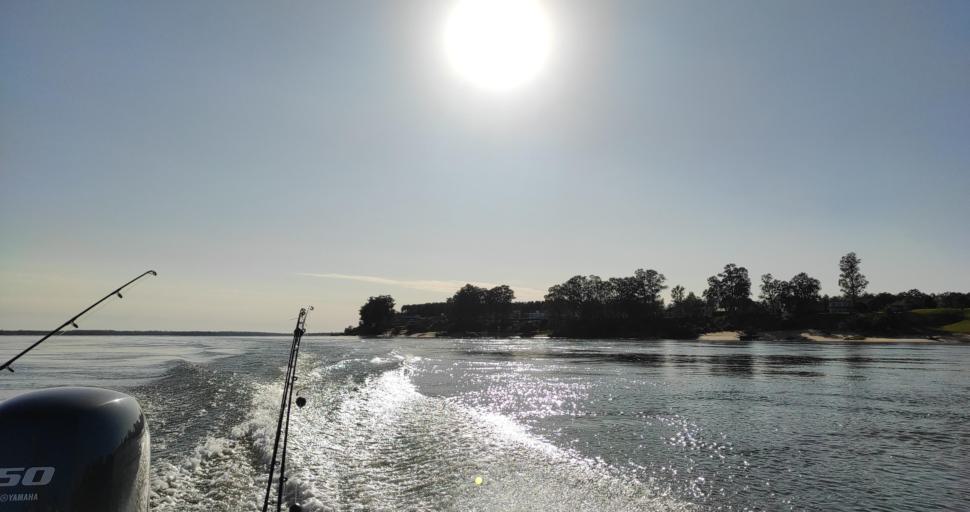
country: AR
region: Corrientes
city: Ituzaingo
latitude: -27.6011
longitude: -56.8202
